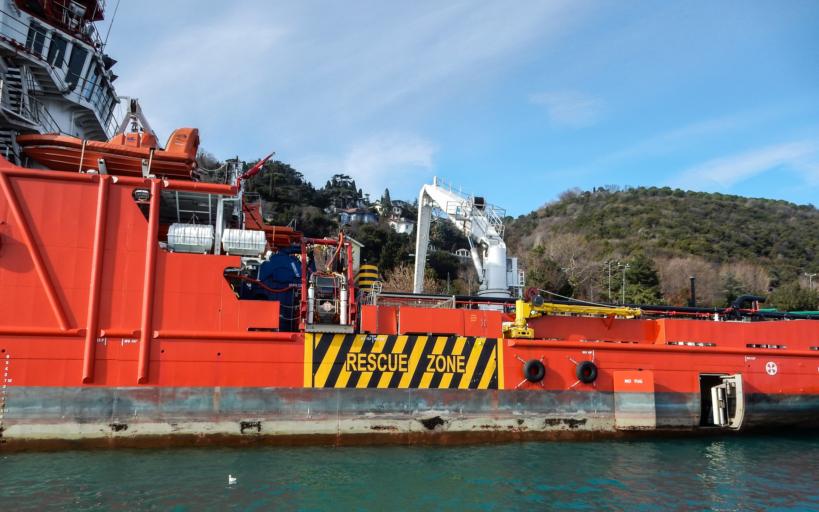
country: TR
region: Istanbul
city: UEskuedar
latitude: 41.0531
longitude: 29.0353
